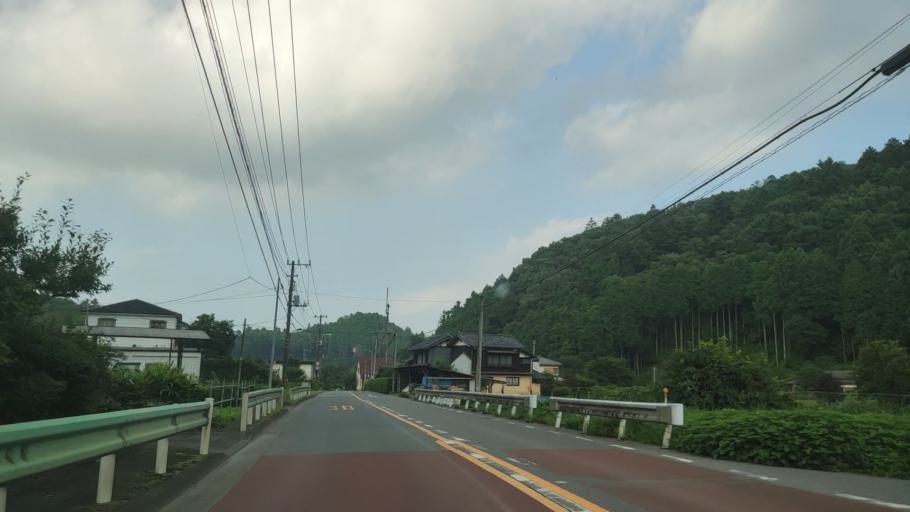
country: JP
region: Tokyo
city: Ome
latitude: 35.8270
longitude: 139.2591
